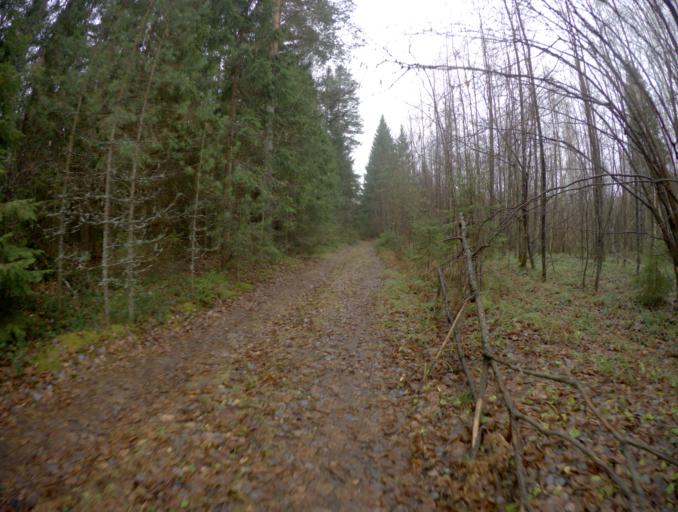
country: RU
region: Vladimir
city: Golovino
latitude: 56.0096
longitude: 40.4838
